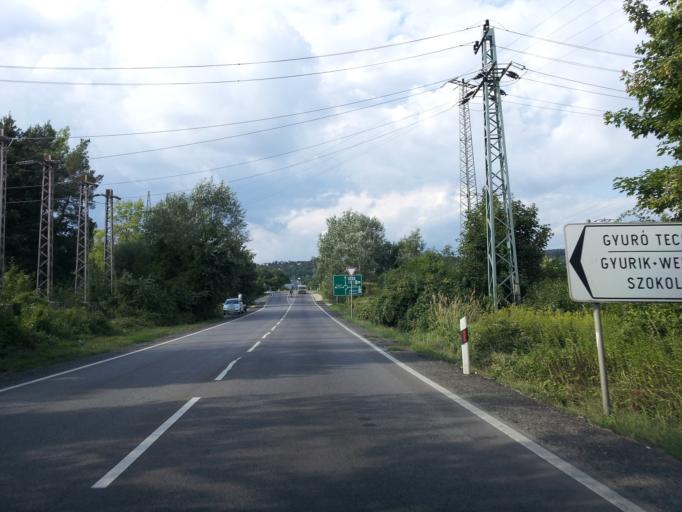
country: HU
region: Pest
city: Vac
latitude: 47.8128
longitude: 19.0934
